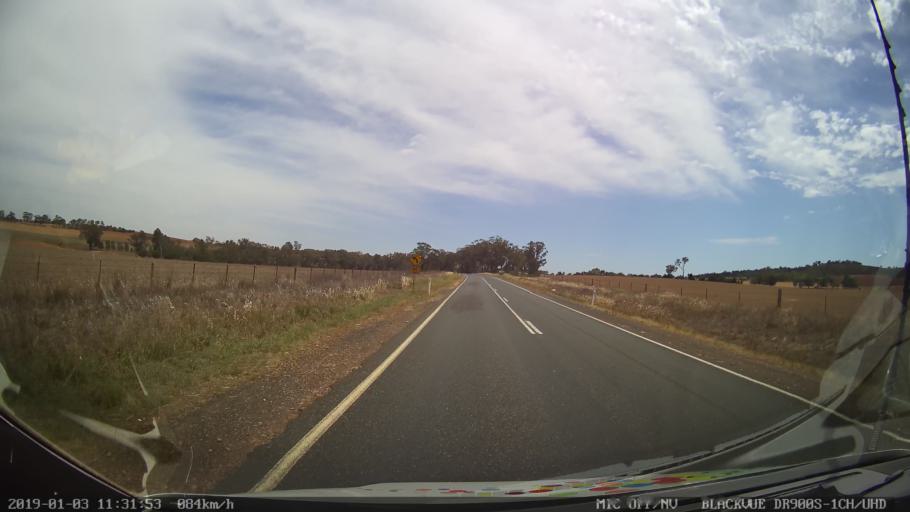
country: AU
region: New South Wales
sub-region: Weddin
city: Grenfell
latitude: -33.9651
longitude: 148.1813
